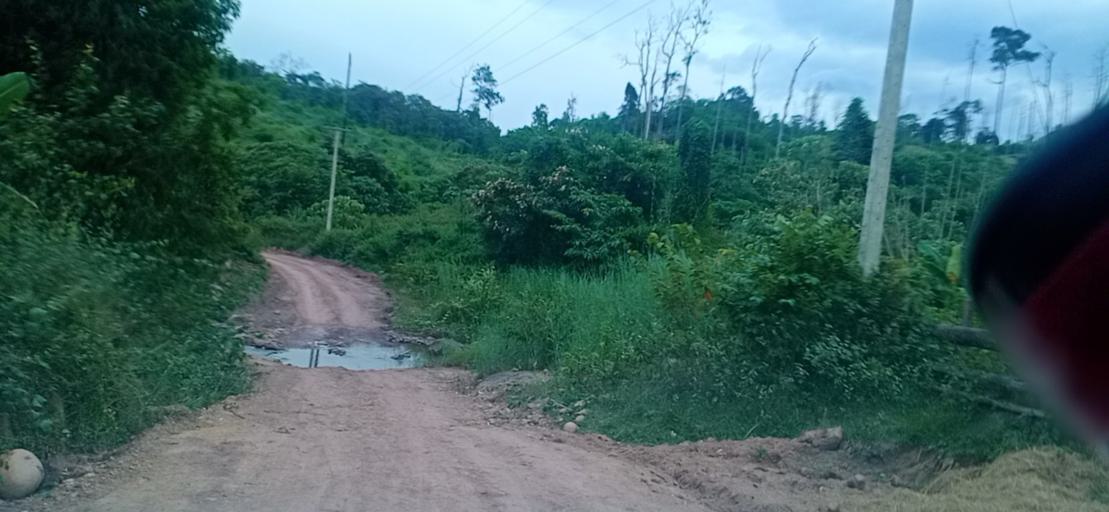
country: TH
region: Changwat Bueng Kan
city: Pak Khat
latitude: 18.5508
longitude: 103.4245
